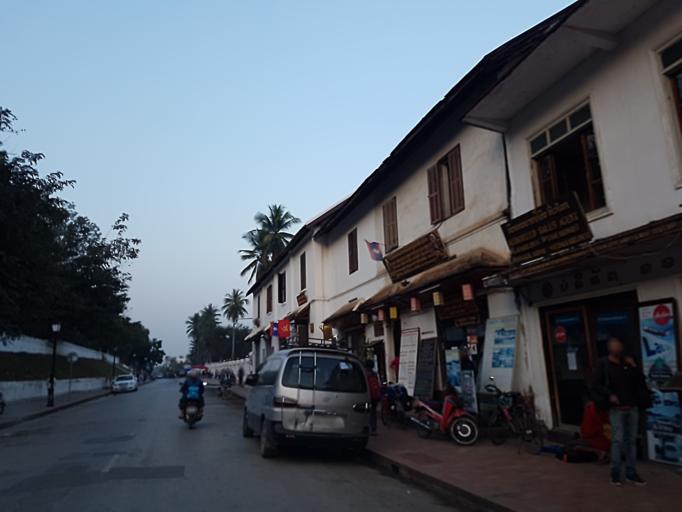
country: LA
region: Louangphabang
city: Louangphabang
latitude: 19.8921
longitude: 102.1373
